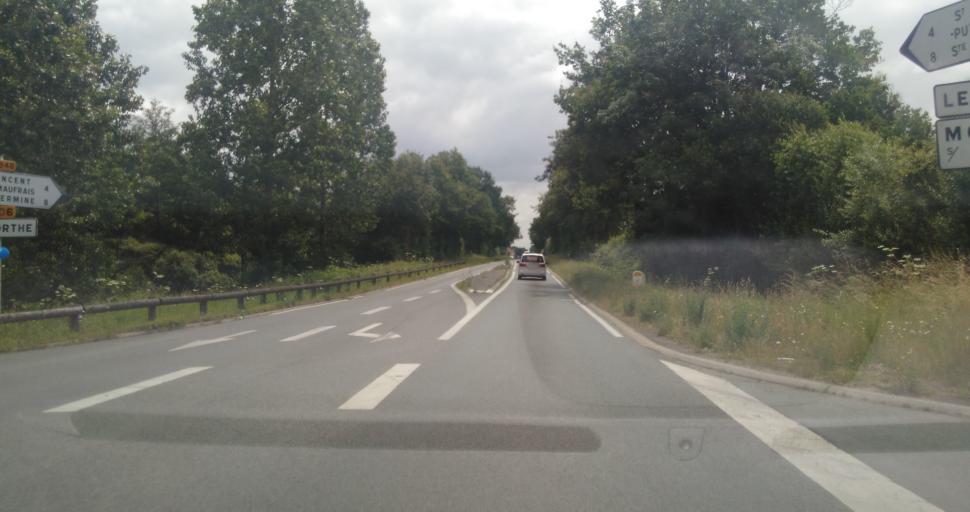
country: FR
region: Pays de la Loire
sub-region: Departement de la Vendee
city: Bournezeau
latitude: 46.6023
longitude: -1.1359
